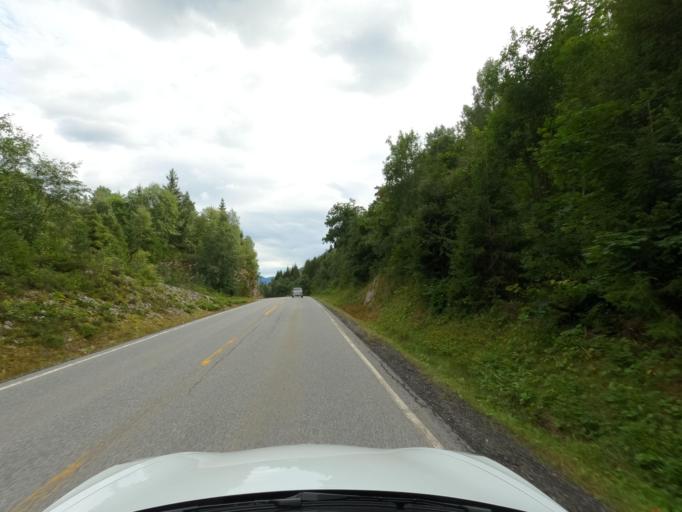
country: NO
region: Telemark
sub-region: Hjartdal
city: Sauland
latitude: 59.8245
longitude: 8.9811
